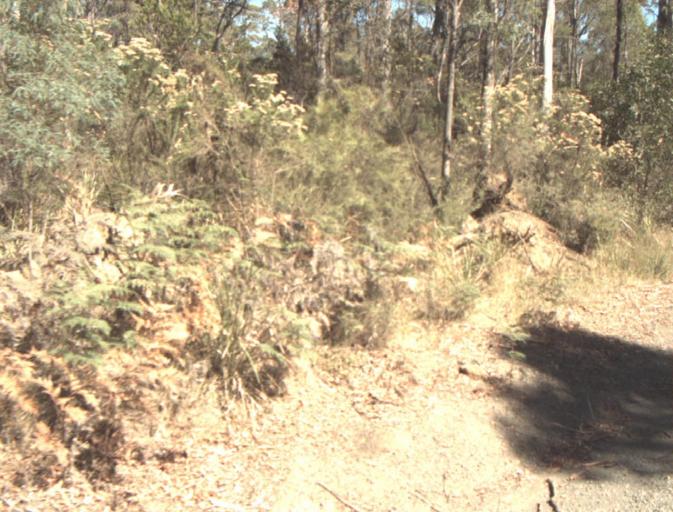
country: AU
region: Tasmania
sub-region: Launceston
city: Mayfield
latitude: -41.3451
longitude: 147.2143
